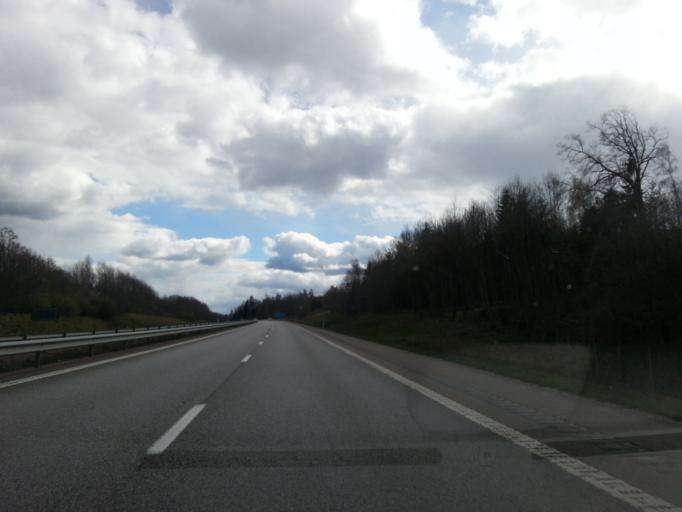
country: SE
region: Vaestra Goetaland
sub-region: Uddevalla Kommun
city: Uddevalla
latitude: 58.3018
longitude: 11.8598
